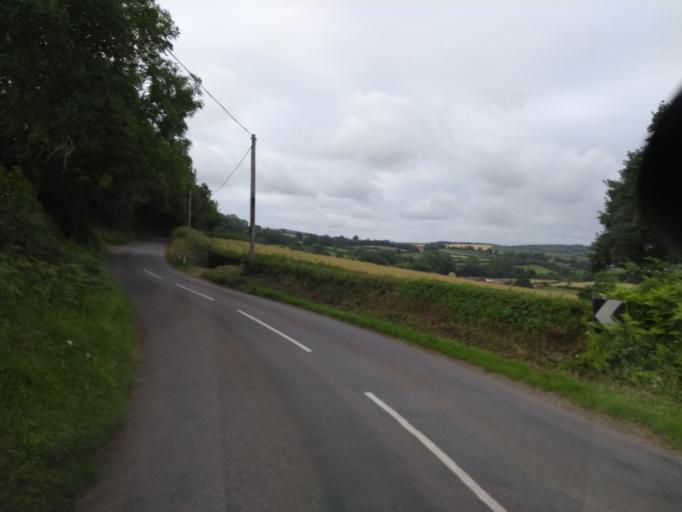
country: GB
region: England
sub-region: Somerset
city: Wiveliscombe
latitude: 51.0574
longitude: -3.2919
